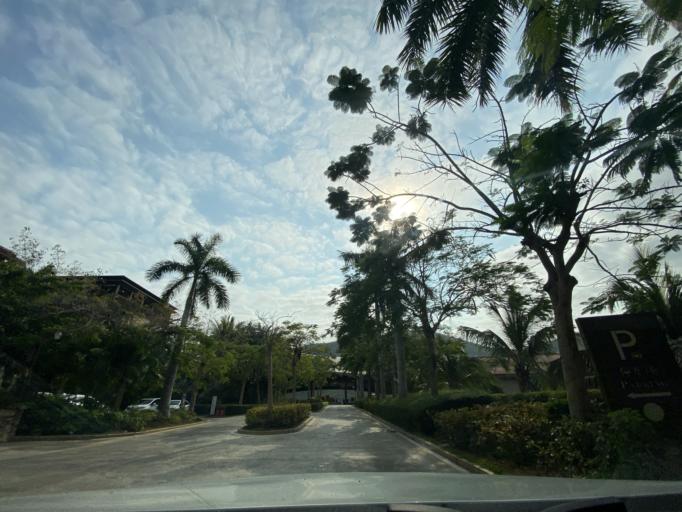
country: CN
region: Hainan
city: Tiandu
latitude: 18.2195
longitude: 109.6125
